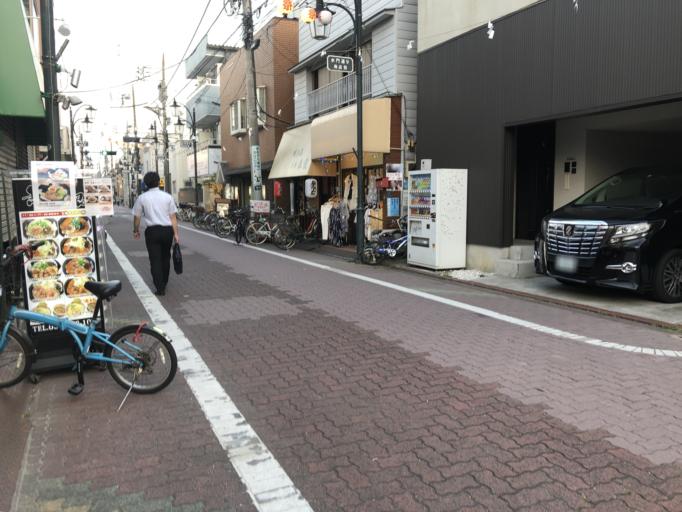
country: JP
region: Kanagawa
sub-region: Kawasaki-shi
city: Kawasaki
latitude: 35.5486
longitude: 139.7183
